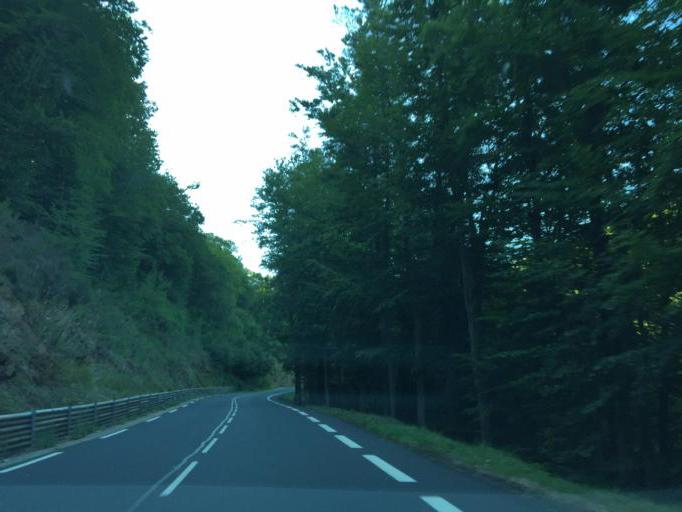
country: FR
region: Auvergne
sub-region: Departement de la Haute-Loire
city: Bains
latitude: 44.9834
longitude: 3.6729
